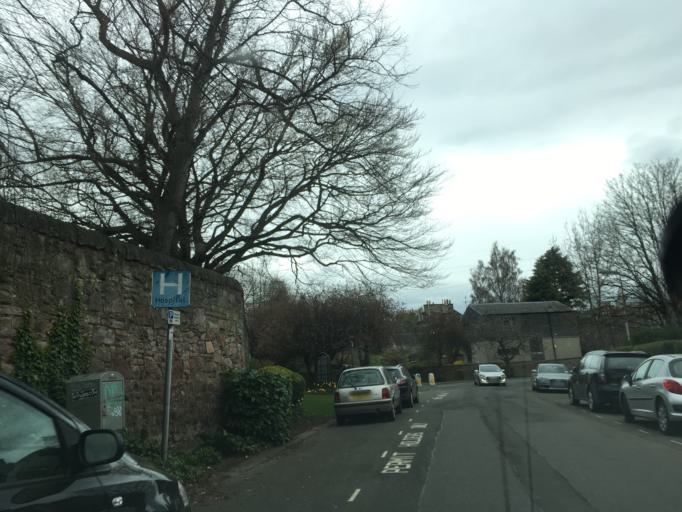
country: GB
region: Scotland
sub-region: Edinburgh
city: Edinburgh
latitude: 55.9274
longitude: -3.2126
